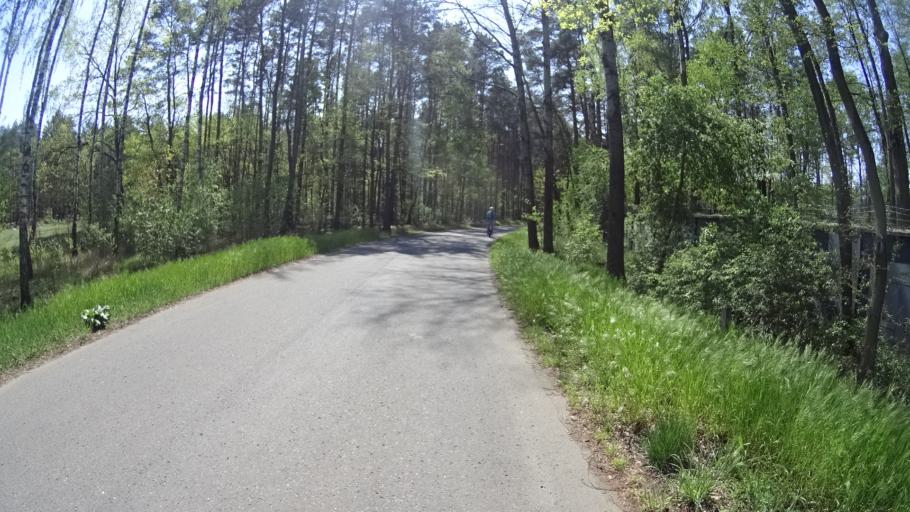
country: PL
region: Masovian Voivodeship
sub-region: Powiat warszawski zachodni
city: Truskaw
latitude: 52.2805
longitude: 20.7254
